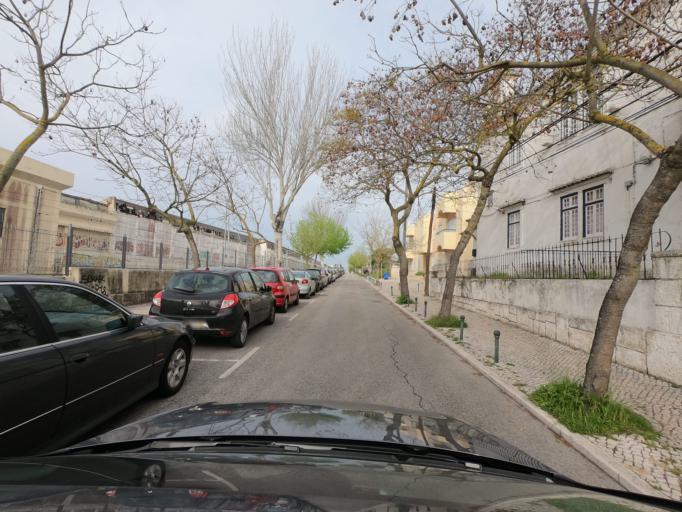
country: PT
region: Lisbon
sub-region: Oeiras
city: Carcavelos
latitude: 38.6887
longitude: -9.3198
